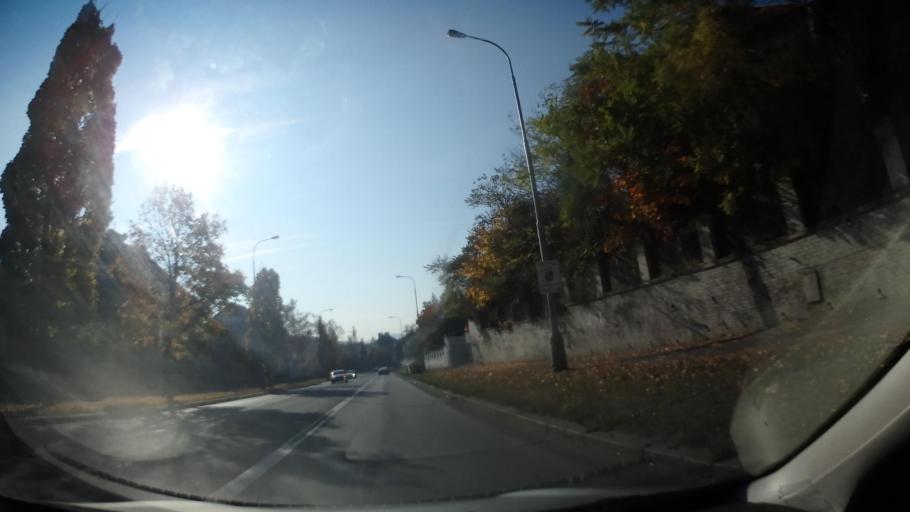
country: CZ
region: Praha
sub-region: Praha 8
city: Karlin
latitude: 50.0756
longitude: 14.4685
